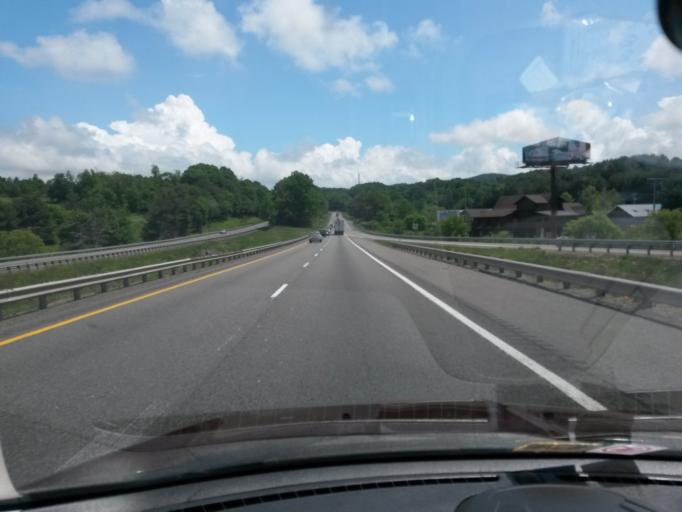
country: US
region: Virginia
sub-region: Carroll County
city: Hillsville
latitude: 36.7441
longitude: -80.7716
